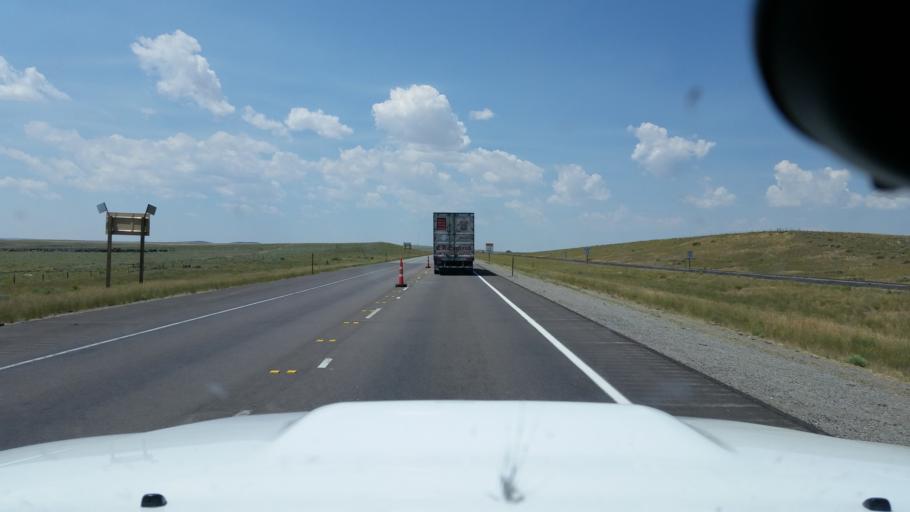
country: US
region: Wyoming
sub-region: Carbon County
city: Saratoga
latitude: 41.7426
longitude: -106.7805
